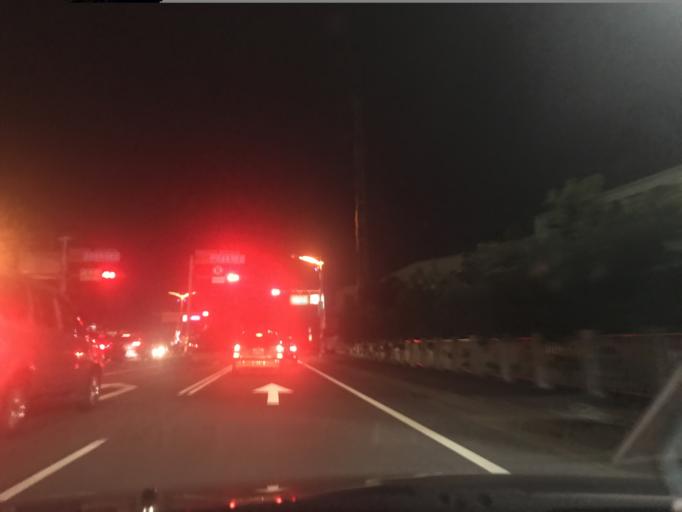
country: TW
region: Taiwan
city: Taoyuan City
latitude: 24.9821
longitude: 121.2364
